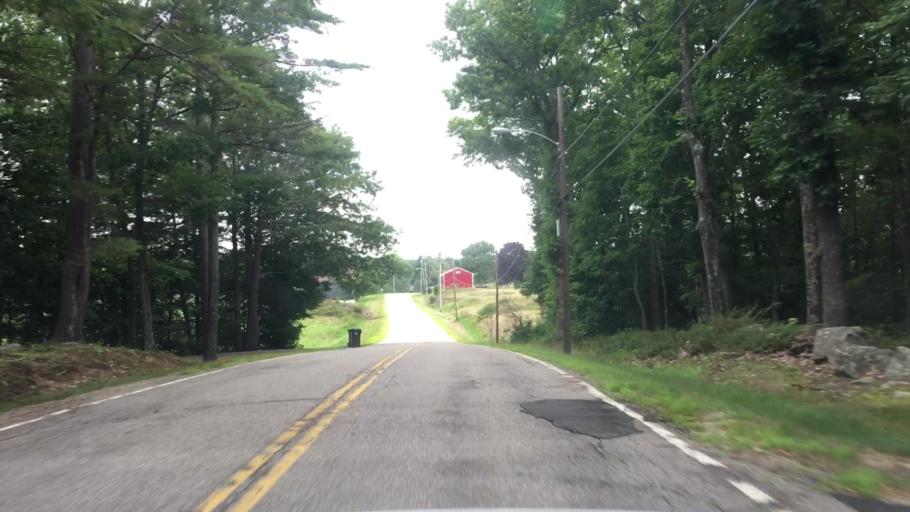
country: US
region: Maine
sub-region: York County
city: Biddeford
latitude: 43.5122
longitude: -70.5096
